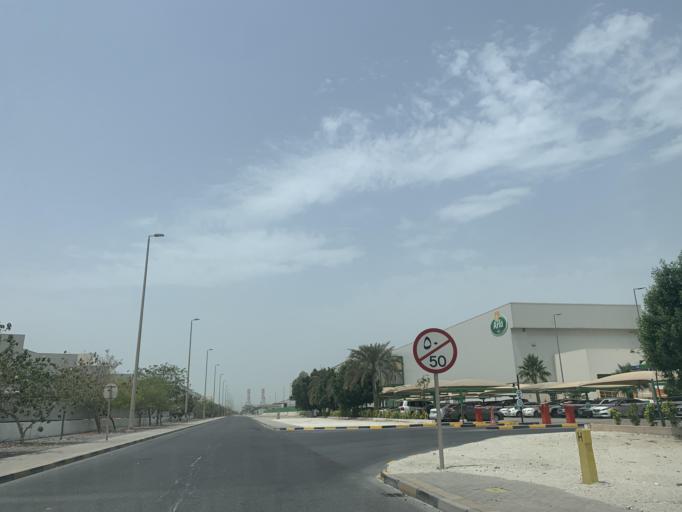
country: BH
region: Muharraq
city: Al Hadd
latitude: 26.2163
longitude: 50.6738
